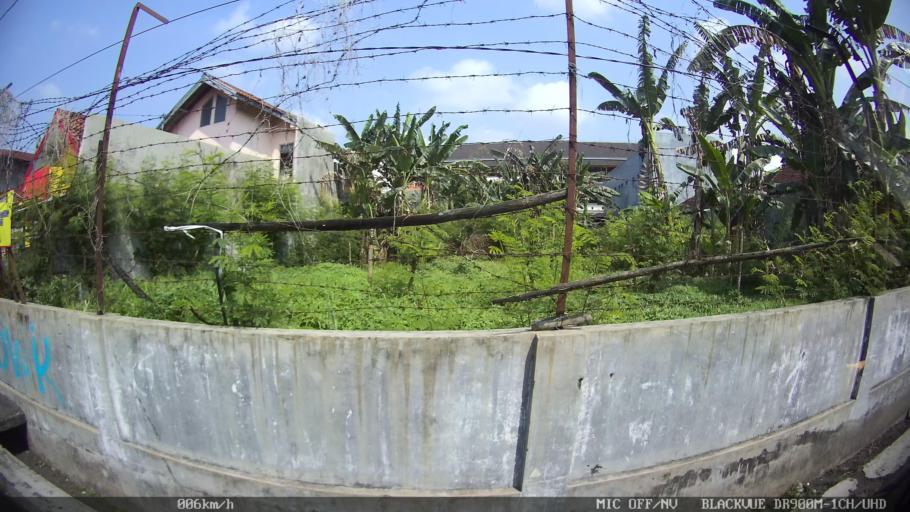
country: ID
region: Daerah Istimewa Yogyakarta
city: Yogyakarta
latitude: -7.8096
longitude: 110.3899
